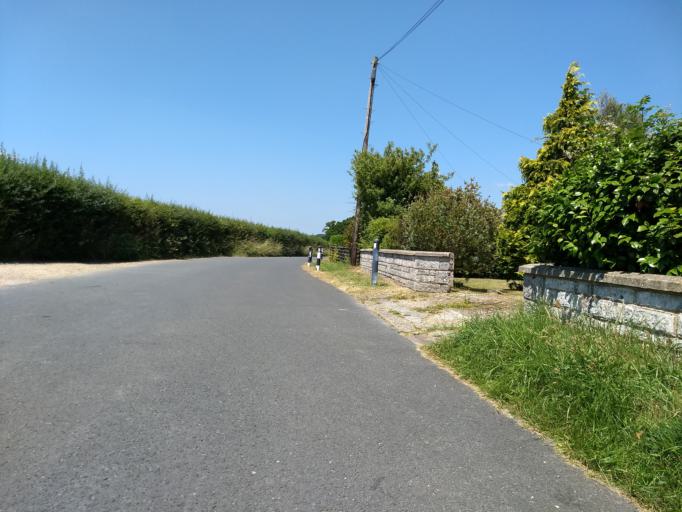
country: GB
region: England
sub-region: Isle of Wight
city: Shalfleet
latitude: 50.7128
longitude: -1.3612
